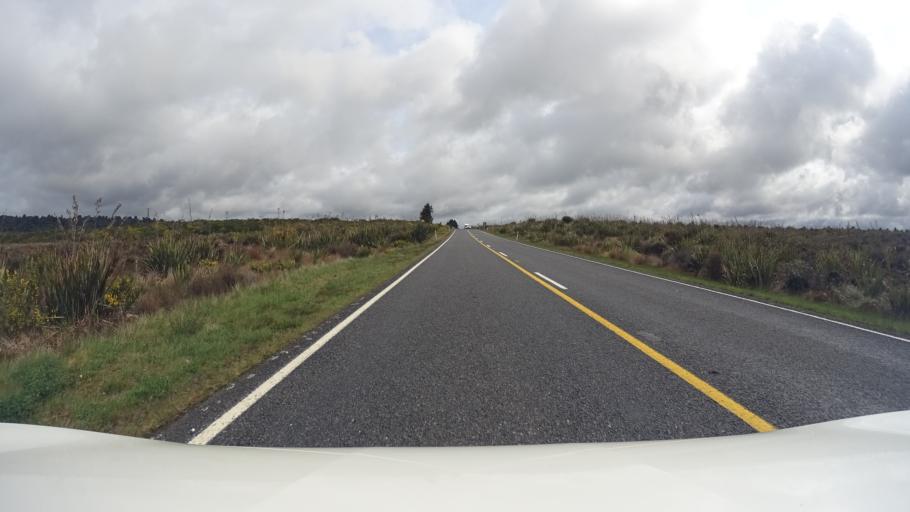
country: NZ
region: Manawatu-Wanganui
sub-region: Ruapehu District
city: Waiouru
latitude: -39.1889
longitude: 175.4018
